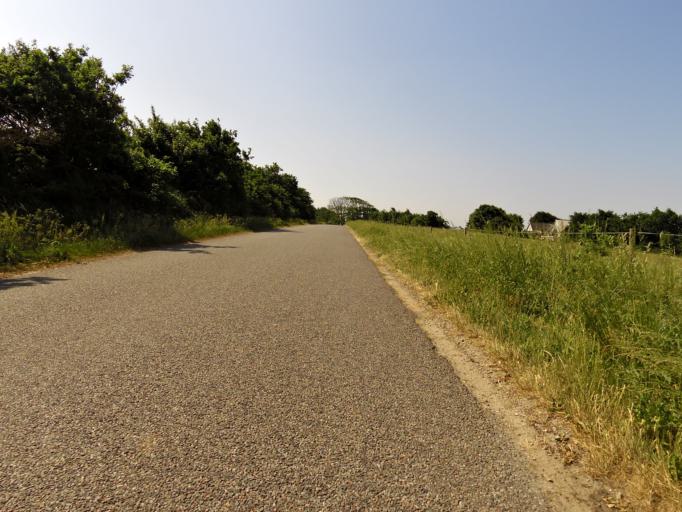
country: DK
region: Central Jutland
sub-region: Holstebro Kommune
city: Vinderup
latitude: 56.4754
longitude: 8.8182
